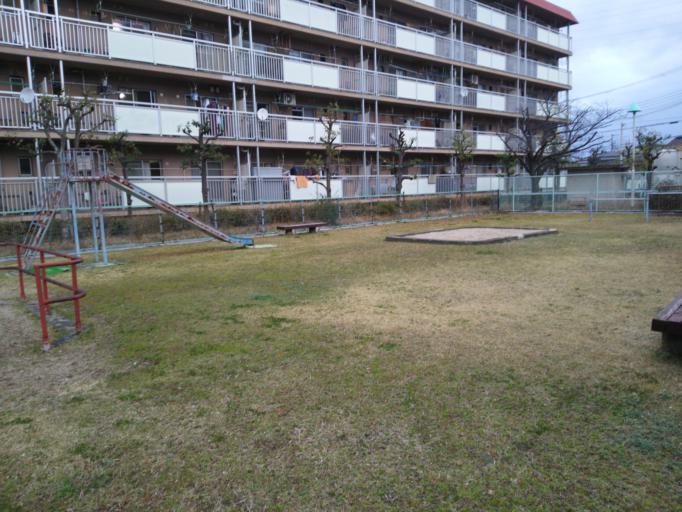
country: JP
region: Hyogo
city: Itami
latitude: 34.7675
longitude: 135.3856
